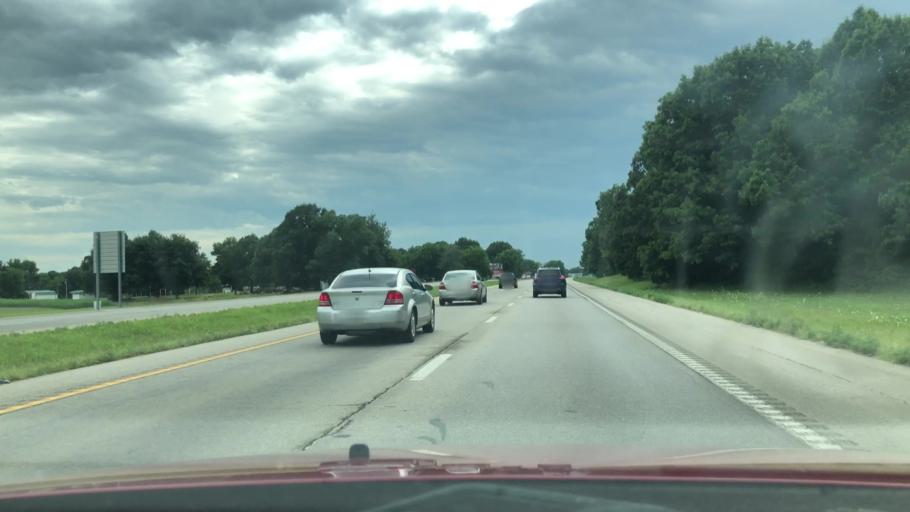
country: US
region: Missouri
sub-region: Greene County
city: Republic
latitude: 37.1440
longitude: -93.4327
